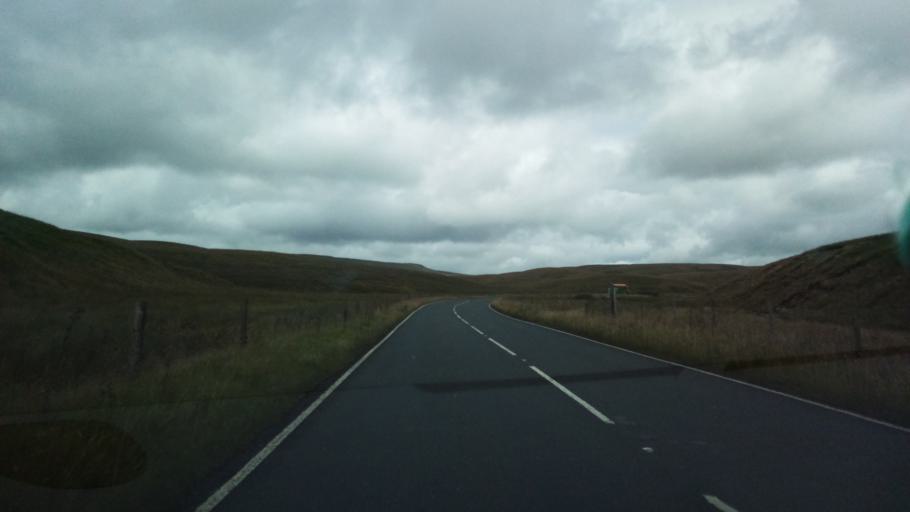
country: GB
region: England
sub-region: North Yorkshire
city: Settle
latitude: 54.2312
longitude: -2.3191
